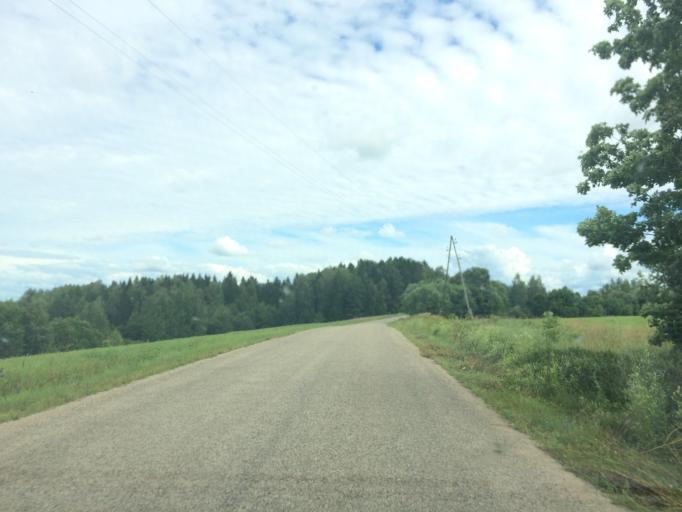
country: LV
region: Rezekne
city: Rezekne
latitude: 56.5651
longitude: 27.4533
